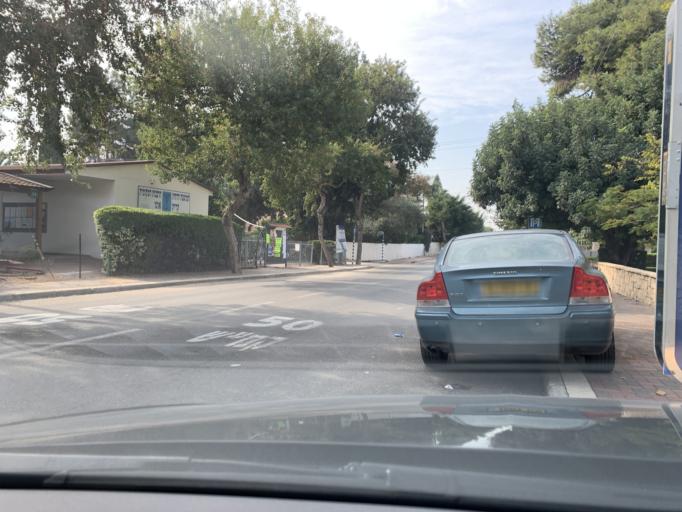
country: IL
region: Central District
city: Ganne Tiqwa
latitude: 32.0607
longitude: 34.8573
